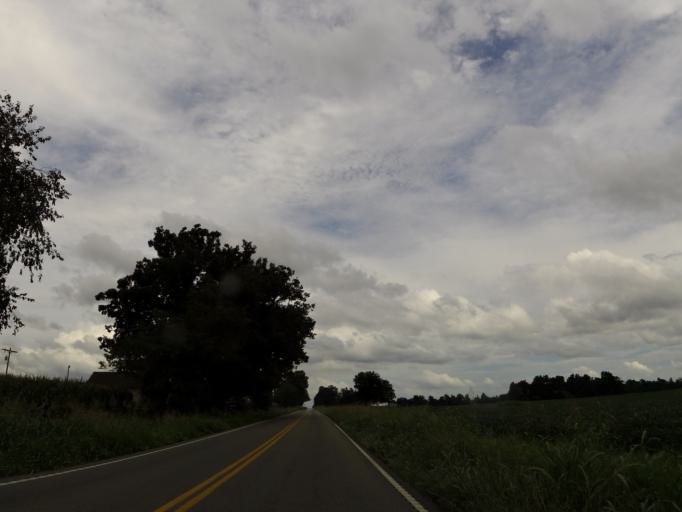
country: US
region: Kentucky
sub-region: Ballard County
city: La Center
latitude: 36.9889
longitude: -88.9517
